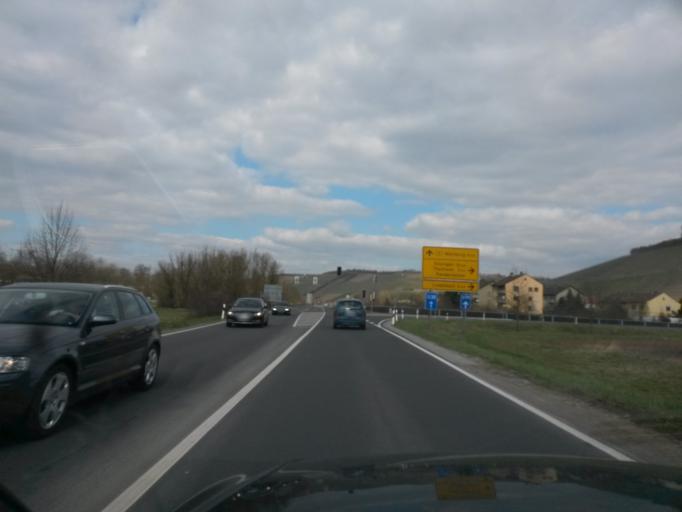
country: DE
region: Bavaria
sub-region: Regierungsbezirk Unterfranken
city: Randersacker
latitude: 49.7520
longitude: 9.9855
